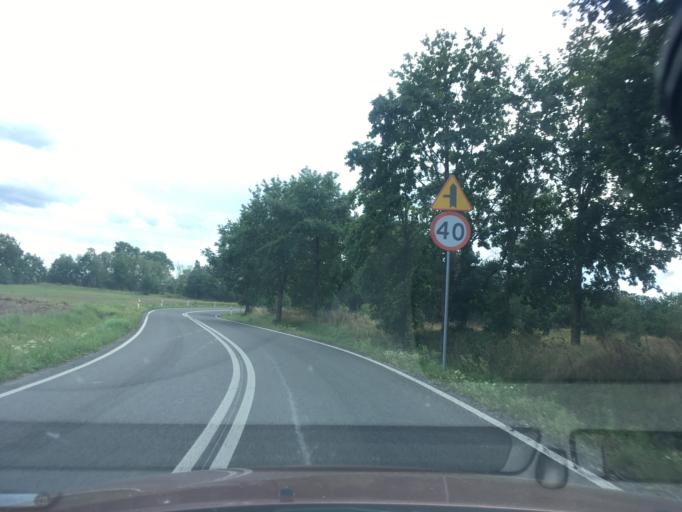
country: PL
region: Lower Silesian Voivodeship
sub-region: Powiat zgorzelecki
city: Piensk
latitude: 51.2182
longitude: 15.0212
